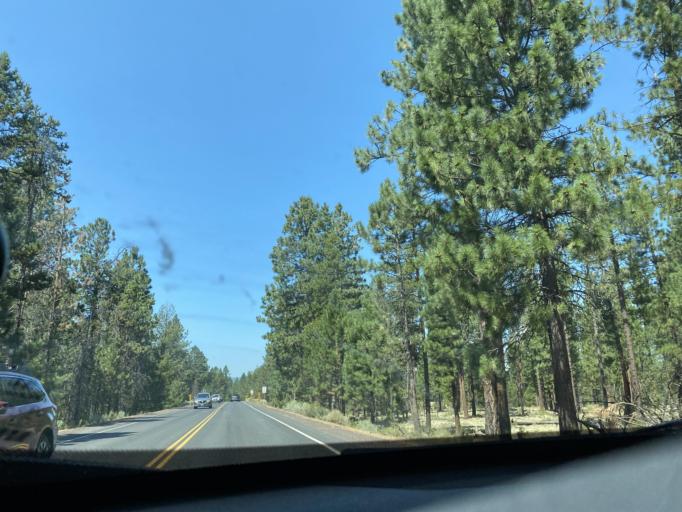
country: US
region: Oregon
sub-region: Deschutes County
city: Sunriver
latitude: 43.8932
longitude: -121.4132
